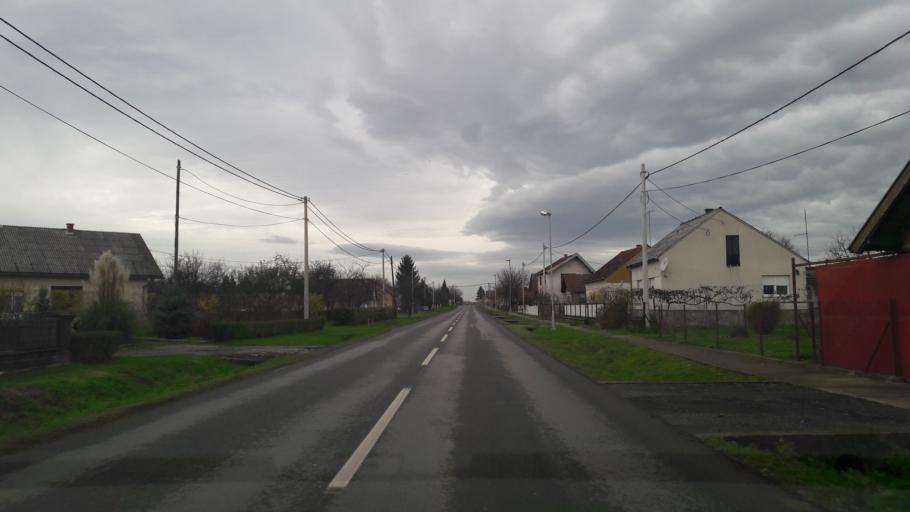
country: HR
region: Osjecko-Baranjska
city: Velimirovac
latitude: 45.5367
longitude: 18.0716
